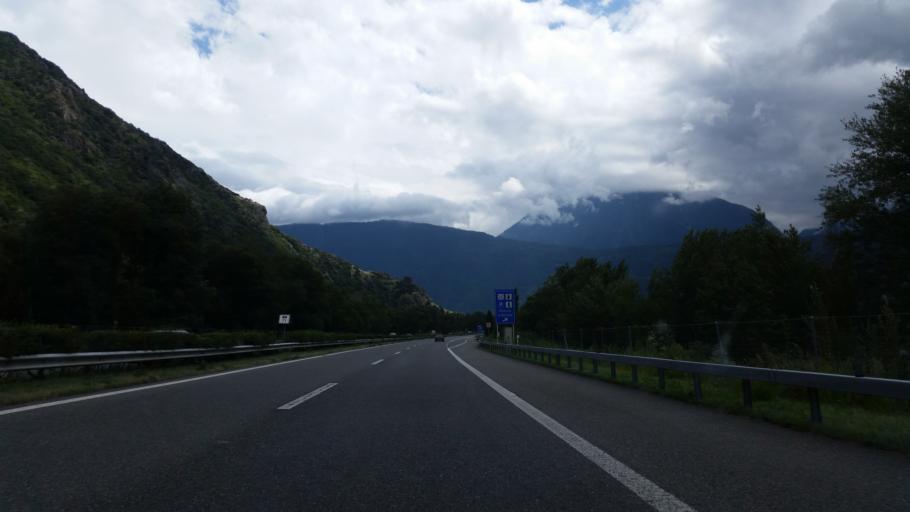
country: CH
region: Valais
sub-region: Saint-Maurice District
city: Vernayaz
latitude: 46.1317
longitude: 7.0569
